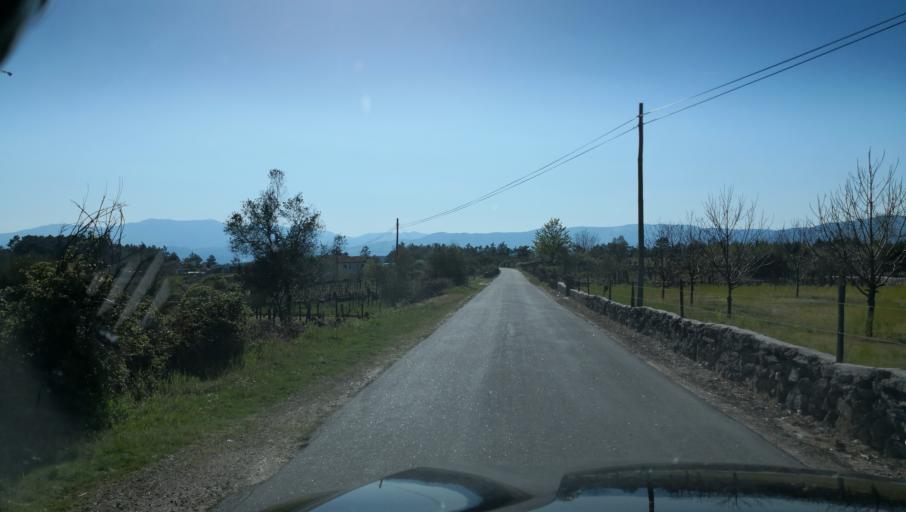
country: PT
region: Vila Real
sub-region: Sabrosa
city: Sabrosa
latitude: 41.2946
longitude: -7.6540
